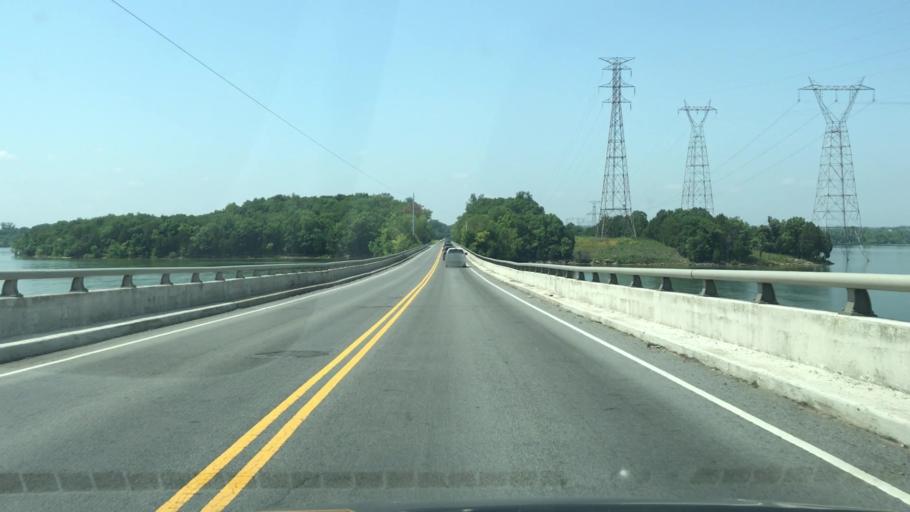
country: US
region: Tennessee
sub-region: Rutherford County
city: La Vergne
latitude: 36.0840
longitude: -86.5656
